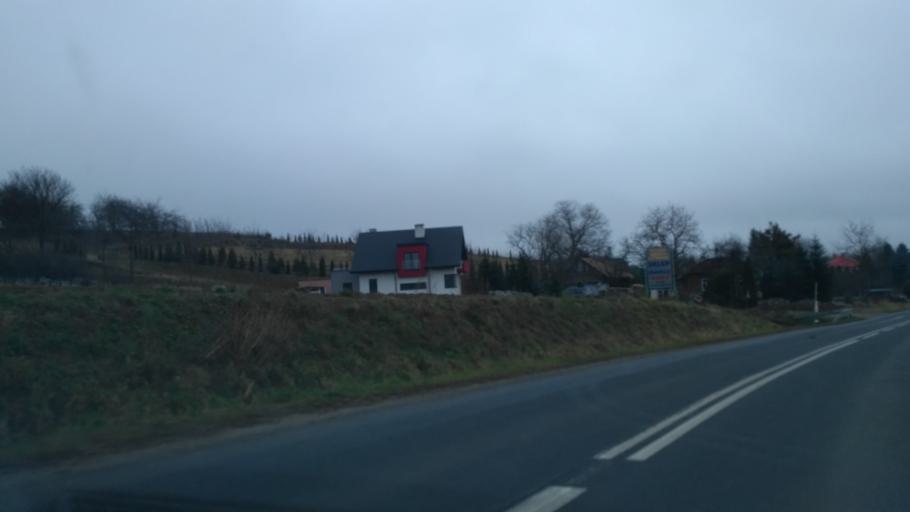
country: PL
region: Subcarpathian Voivodeship
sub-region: Powiat jaroslawski
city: Pruchnik
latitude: 49.9076
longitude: 22.5290
